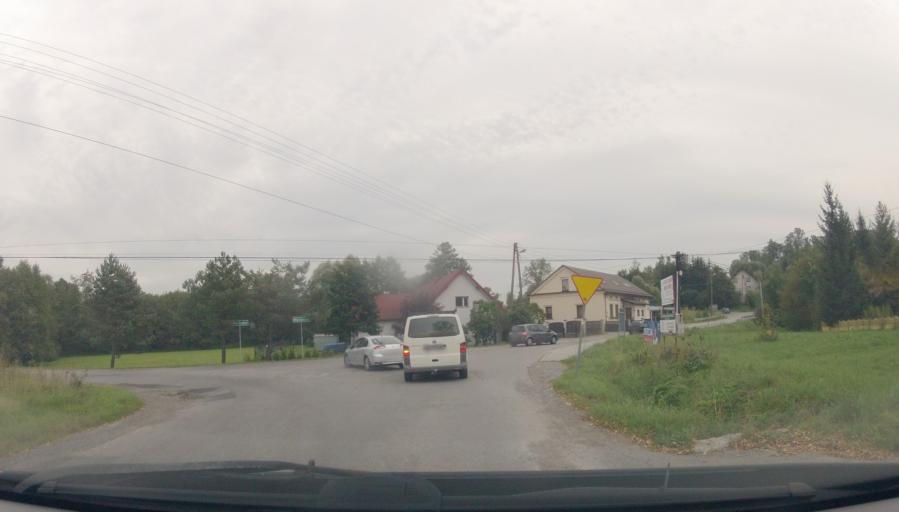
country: PL
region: Lesser Poland Voivodeship
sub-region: Powiat wielicki
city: Pawlikowice
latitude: 49.9553
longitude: 20.0340
